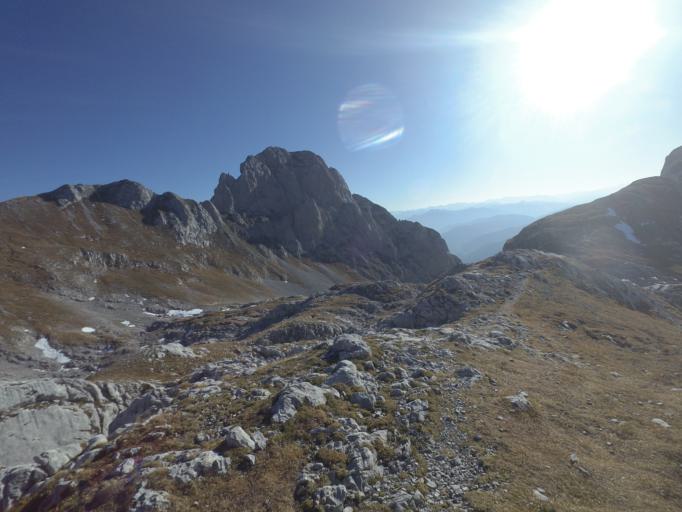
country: AT
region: Salzburg
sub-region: Politischer Bezirk Sankt Johann im Pongau
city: Werfenweng
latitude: 47.4969
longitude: 13.2416
